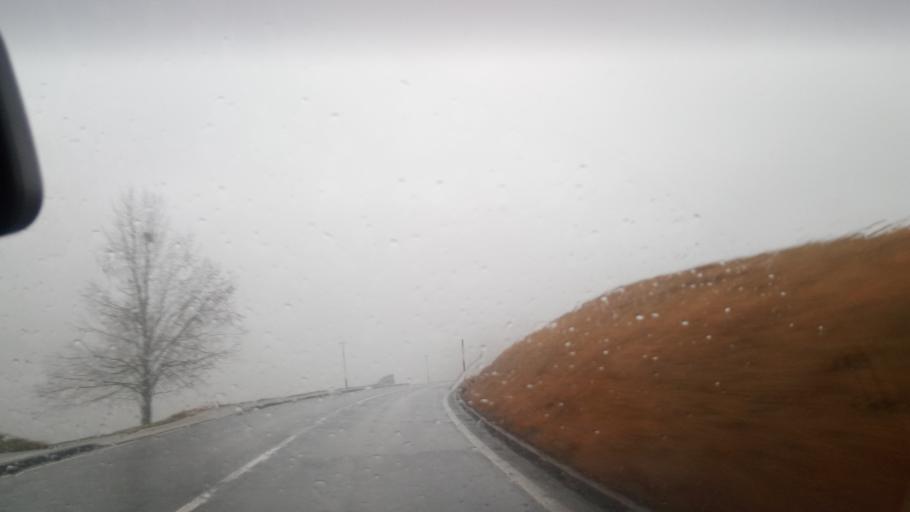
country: AT
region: Carinthia
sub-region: Politischer Bezirk Klagenfurt Land
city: Keutschach am See
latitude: 46.5893
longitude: 14.2102
